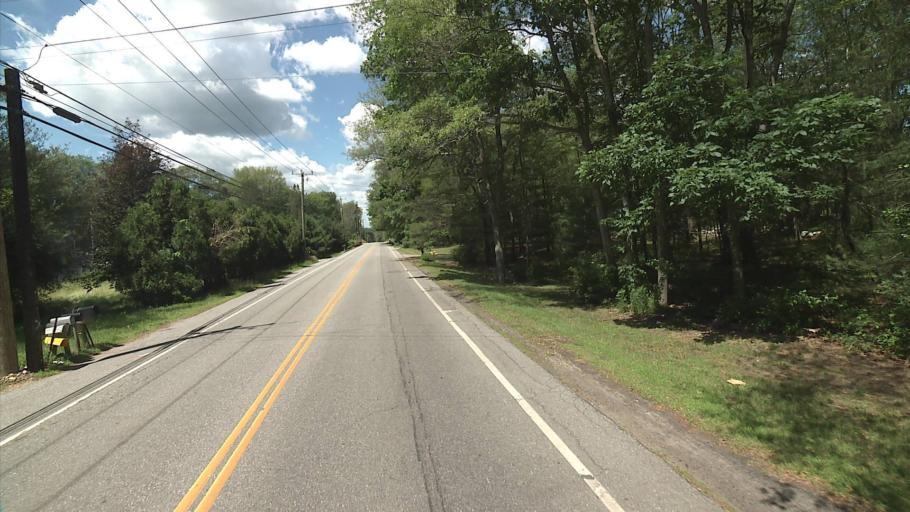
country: US
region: Rhode Island
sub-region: Washington County
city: Ashaway
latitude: 41.4366
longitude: -71.8144
